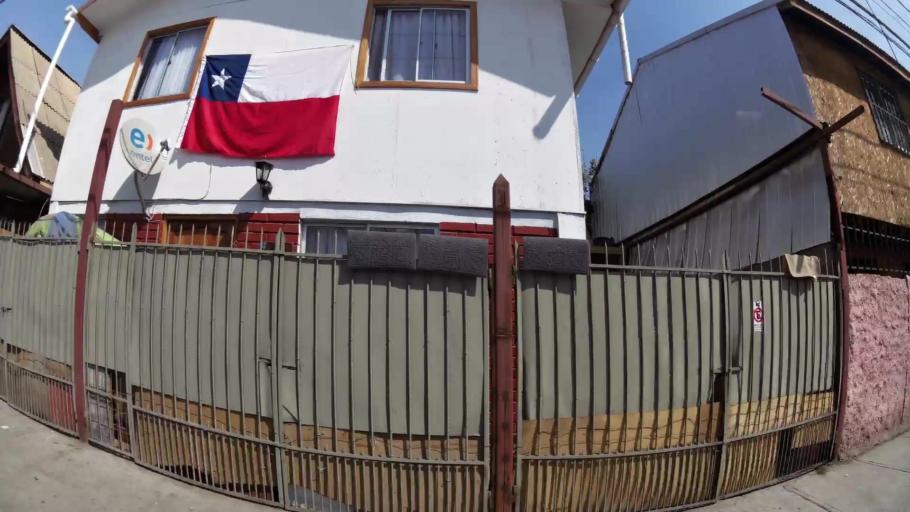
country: CL
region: Santiago Metropolitan
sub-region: Provincia de Santiago
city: Villa Presidente Frei, Nunoa, Santiago, Chile
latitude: -33.5126
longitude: -70.5801
